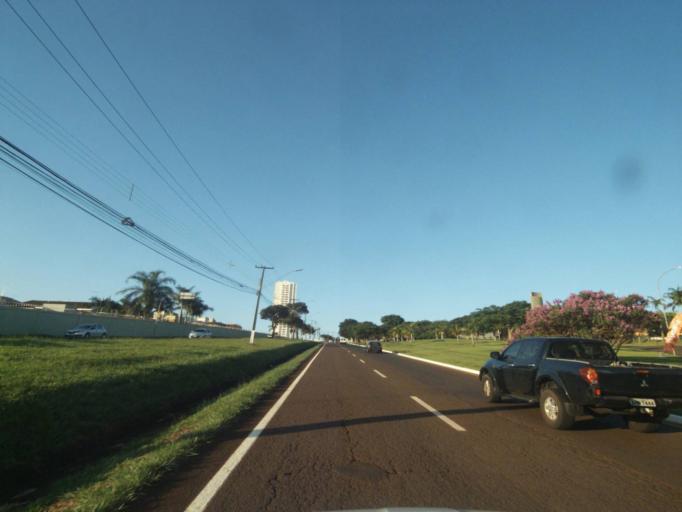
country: BR
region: Parana
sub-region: Londrina
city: Londrina
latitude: -23.3456
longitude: -51.1894
